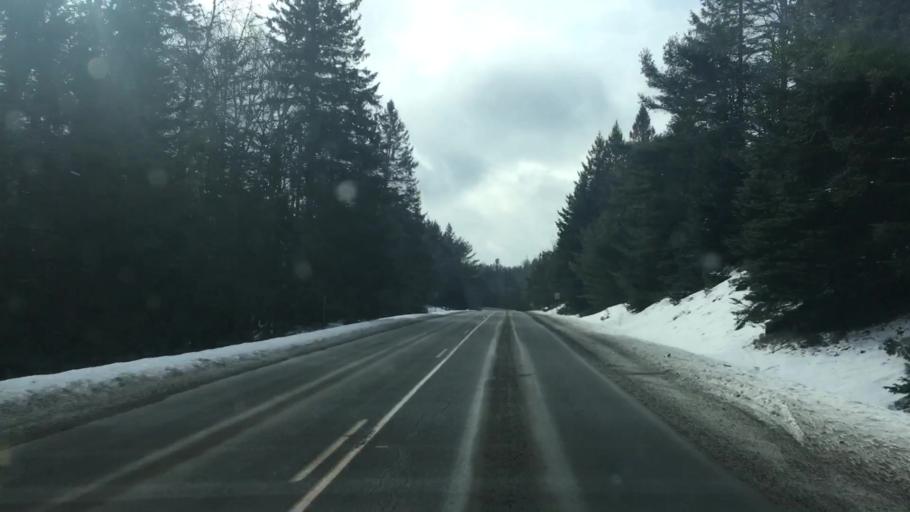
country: US
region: Maine
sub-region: Washington County
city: Calais
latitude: 45.0492
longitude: -67.3264
